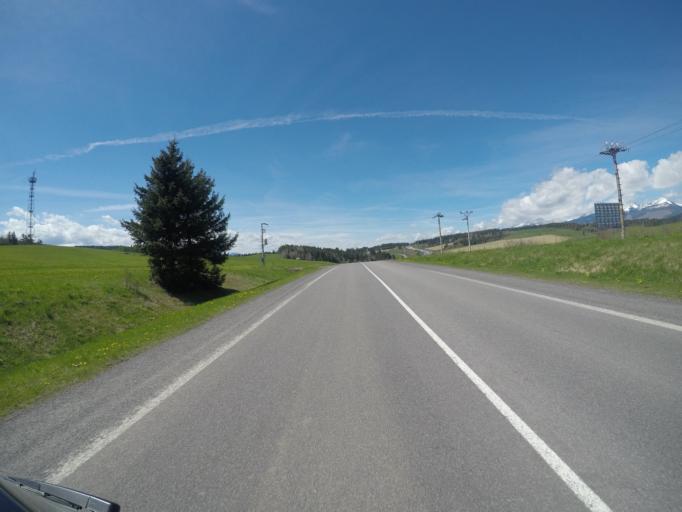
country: SK
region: Presovsky
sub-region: Okres Poprad
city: Strba
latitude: 49.0631
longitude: 19.9572
